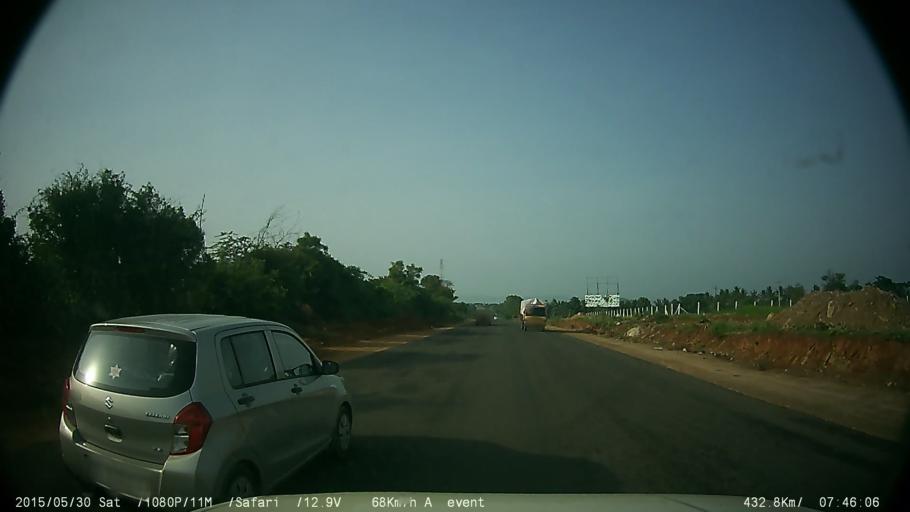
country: IN
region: Karnataka
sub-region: Chamrajnagar
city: Gundlupet
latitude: 11.8872
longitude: 76.6650
